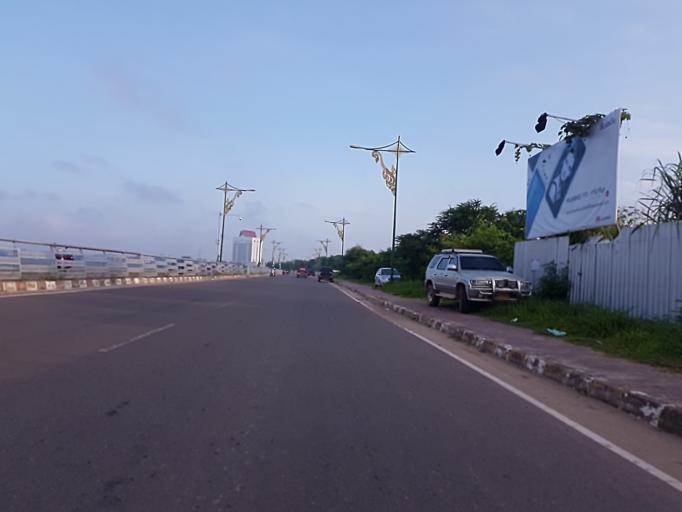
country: LA
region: Vientiane
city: Vientiane
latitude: 17.9466
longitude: 102.6159
